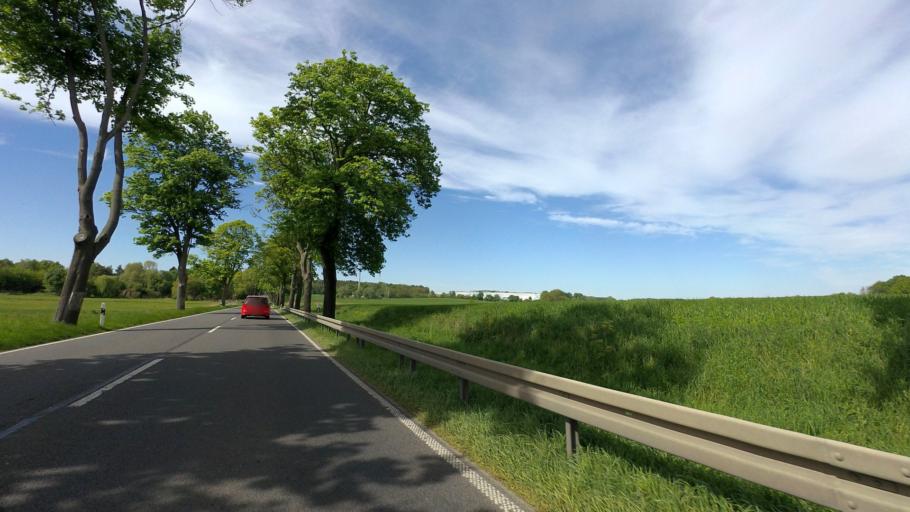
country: DE
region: Brandenburg
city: Rangsdorf
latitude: 52.2860
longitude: 13.4619
